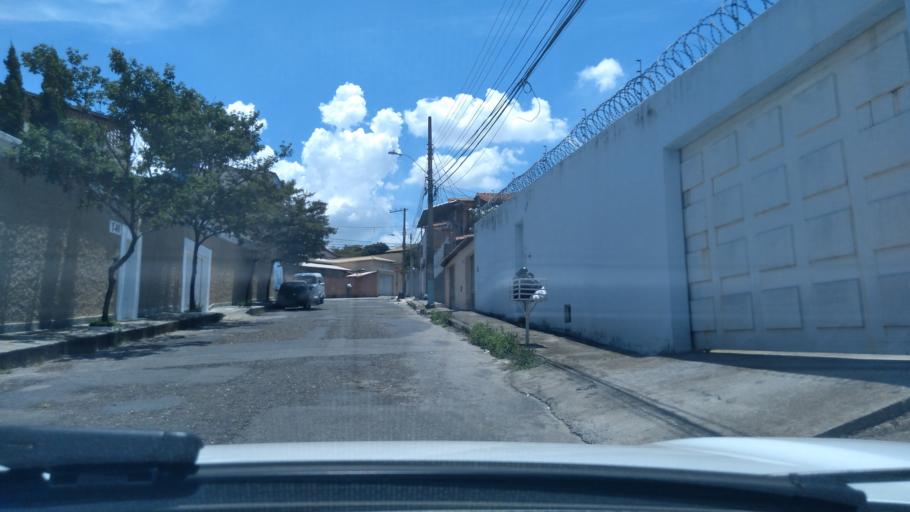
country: BR
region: Minas Gerais
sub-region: Contagem
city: Contagem
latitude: -19.9326
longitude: -43.9989
